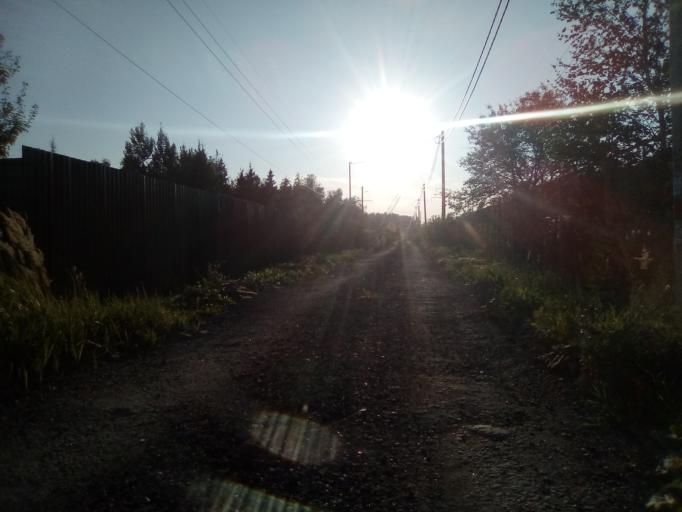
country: RU
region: Moskovskaya
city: Krasnoznamensk
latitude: 55.5807
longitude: 37.0602
